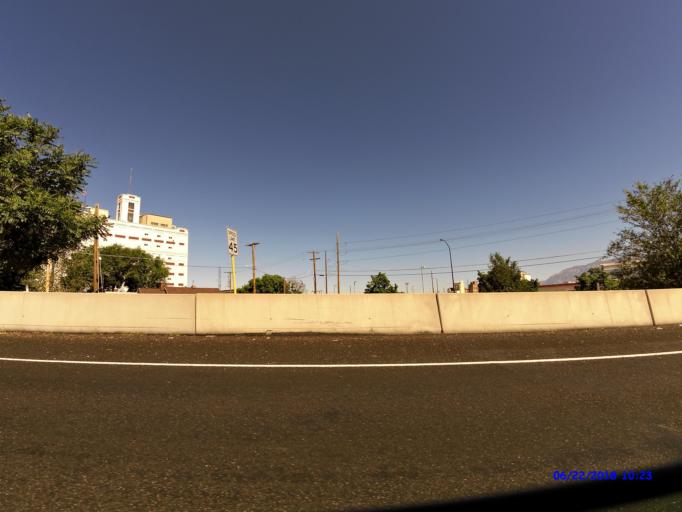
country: US
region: Utah
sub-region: Weber County
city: Ogden
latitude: 41.2100
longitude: -111.9814
